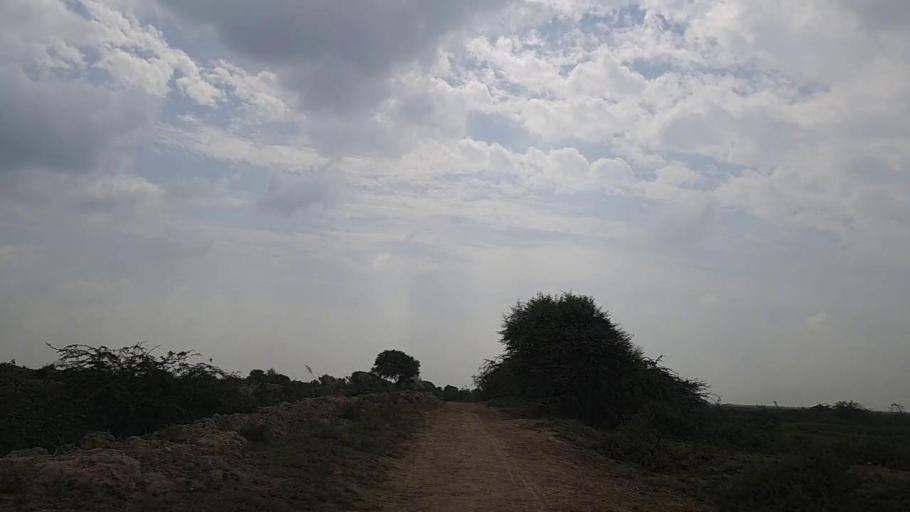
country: PK
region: Sindh
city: Mirpur Batoro
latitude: 24.6192
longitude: 68.1359
